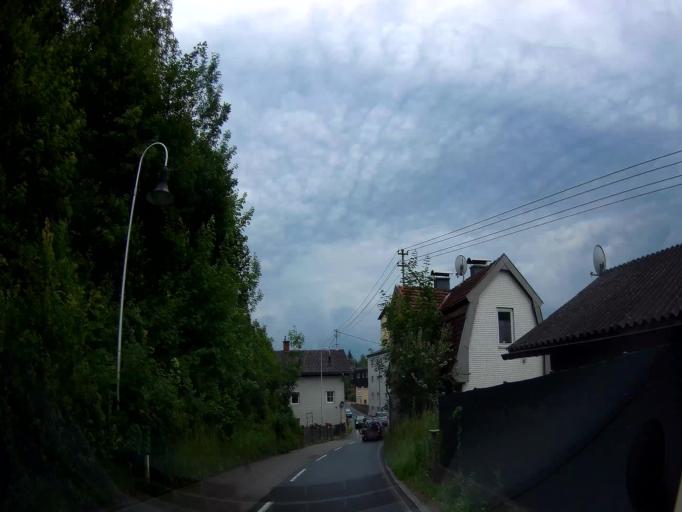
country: AT
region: Salzburg
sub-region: Politischer Bezirk Salzburg-Umgebung
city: Mattsee
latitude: 48.0996
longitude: 13.1493
